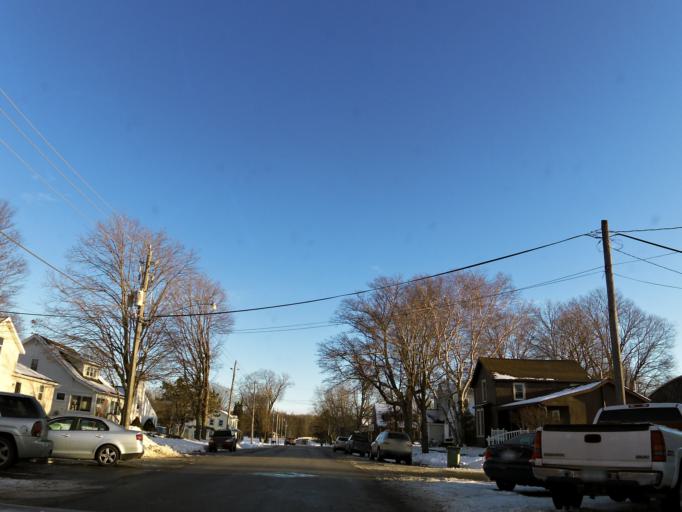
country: US
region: Iowa
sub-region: Butler County
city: Shell Rock
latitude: 42.7099
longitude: -92.5831
